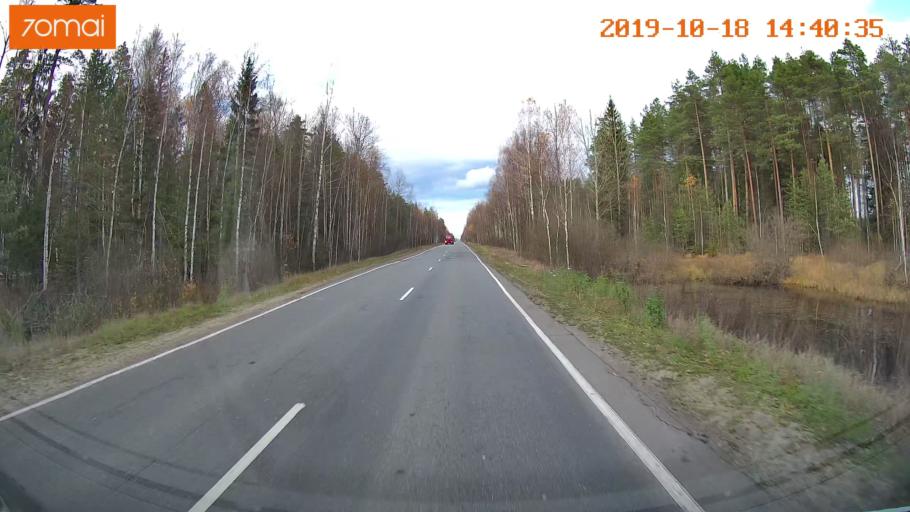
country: RU
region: Vladimir
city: Velikodvorskiy
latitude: 55.2788
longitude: 40.6693
